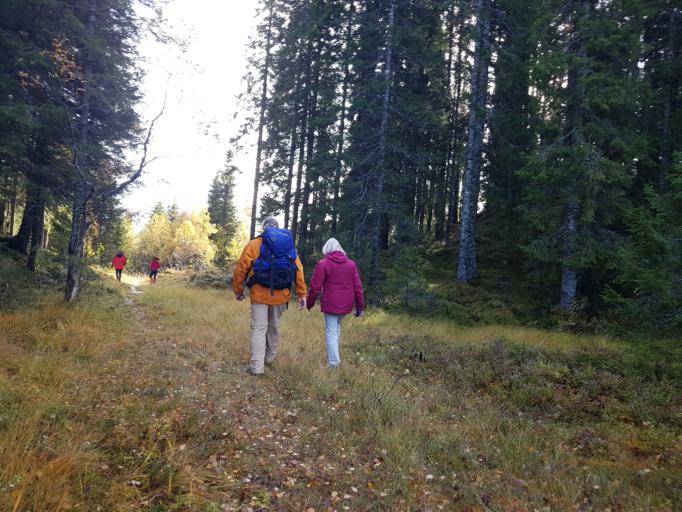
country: NO
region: Sor-Trondelag
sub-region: Trondheim
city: Trondheim
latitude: 63.4245
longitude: 10.2835
